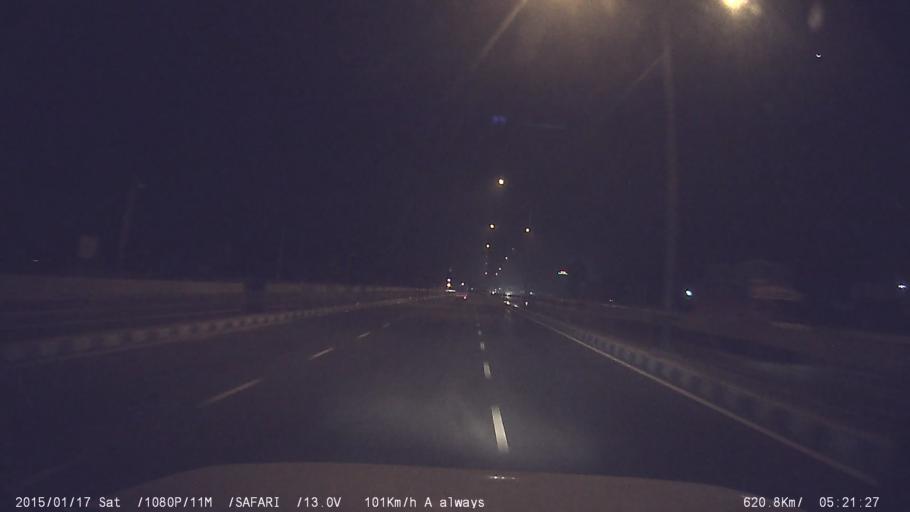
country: IN
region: Tamil Nadu
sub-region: Vellore
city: Katpadi
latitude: 12.9400
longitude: 79.1724
